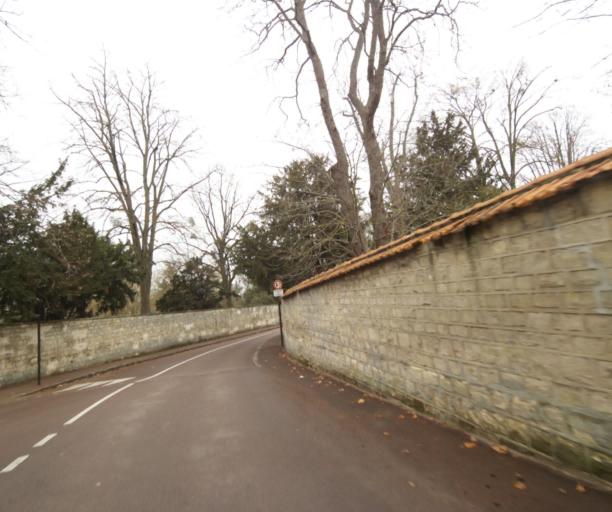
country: FR
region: Ile-de-France
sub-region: Departement des Hauts-de-Seine
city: Rueil-Malmaison
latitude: 48.8704
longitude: 2.1692
